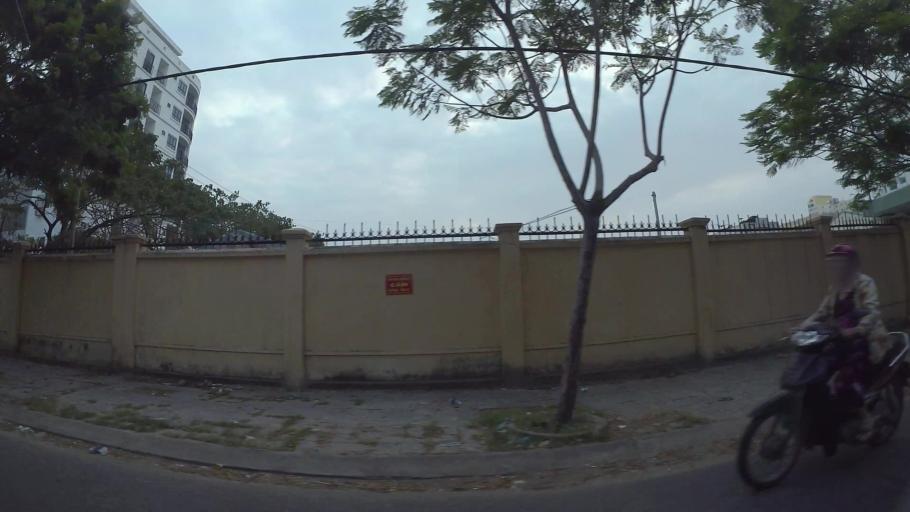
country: VN
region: Da Nang
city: Son Tra
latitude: 16.0536
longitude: 108.2445
